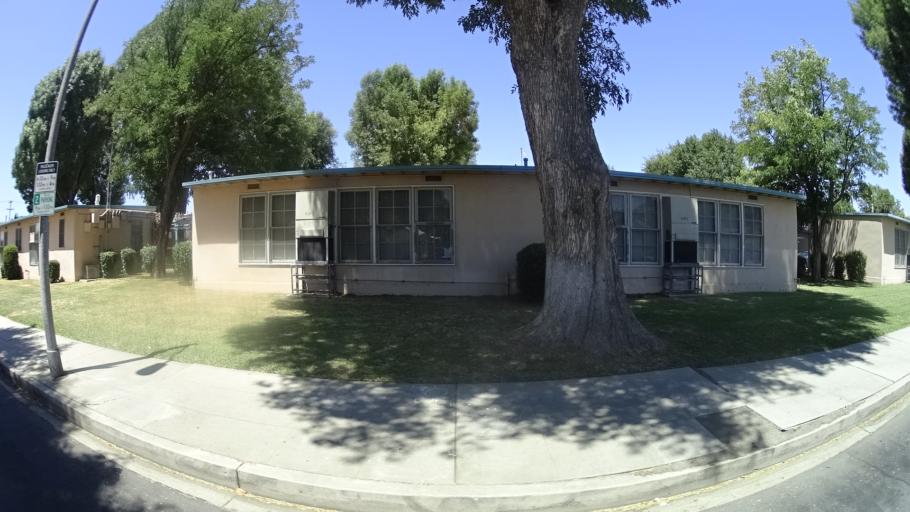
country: US
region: California
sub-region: Los Angeles County
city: Northridge
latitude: 34.1984
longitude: -118.5244
